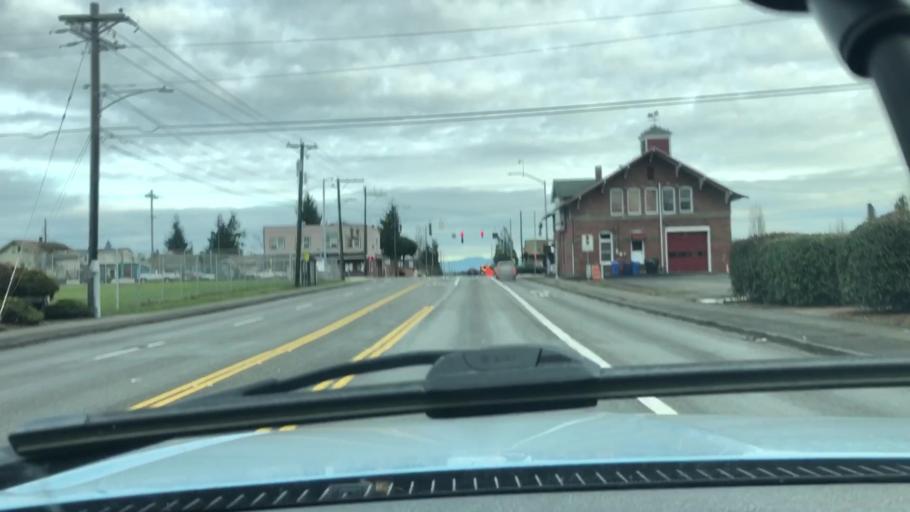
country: US
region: Washington
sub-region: Pierce County
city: Tacoma
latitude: 47.2231
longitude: -122.4223
